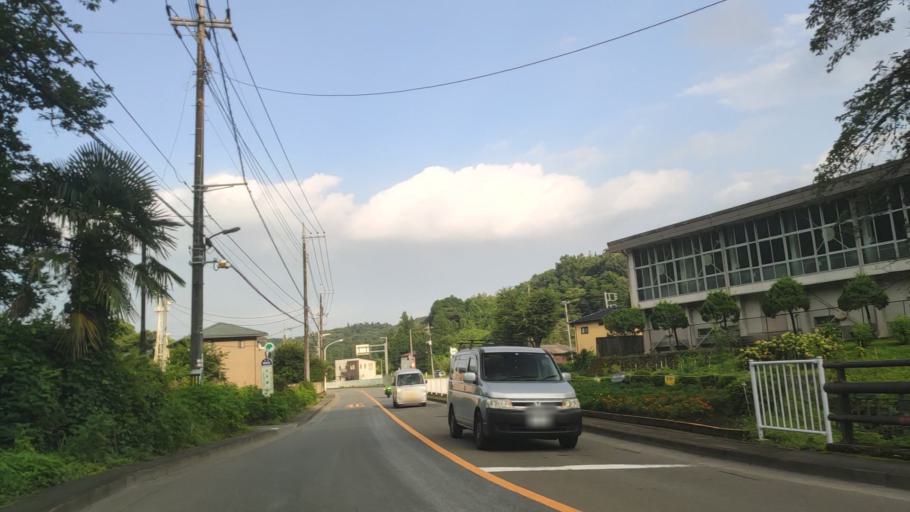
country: JP
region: Saitama
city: Hanno
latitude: 35.8223
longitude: 139.2768
